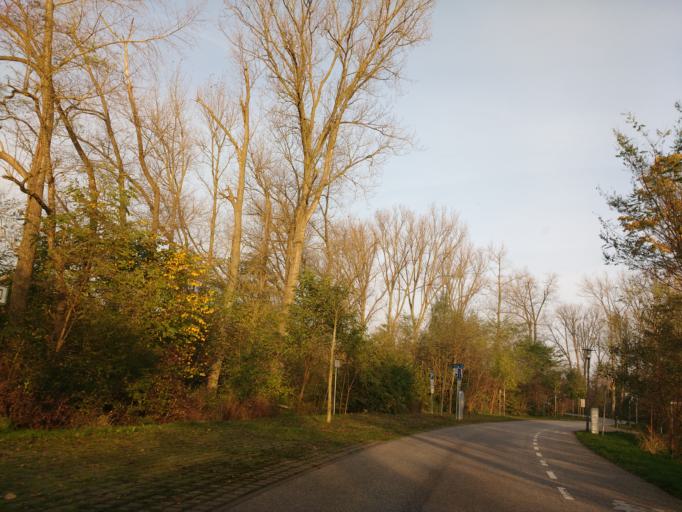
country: DE
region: Mecklenburg-Vorpommern
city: Ostseebad Boltenhagen
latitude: 53.9744
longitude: 11.2447
